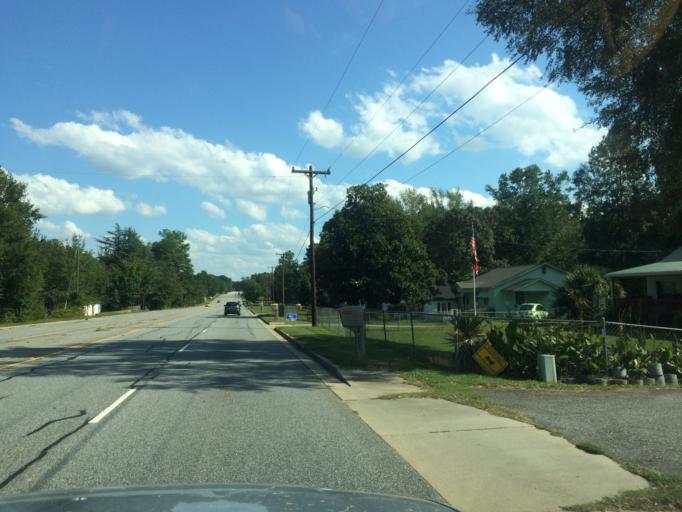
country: US
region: South Carolina
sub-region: Greenwood County
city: Ware Shoals
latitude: 34.4386
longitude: -82.2487
